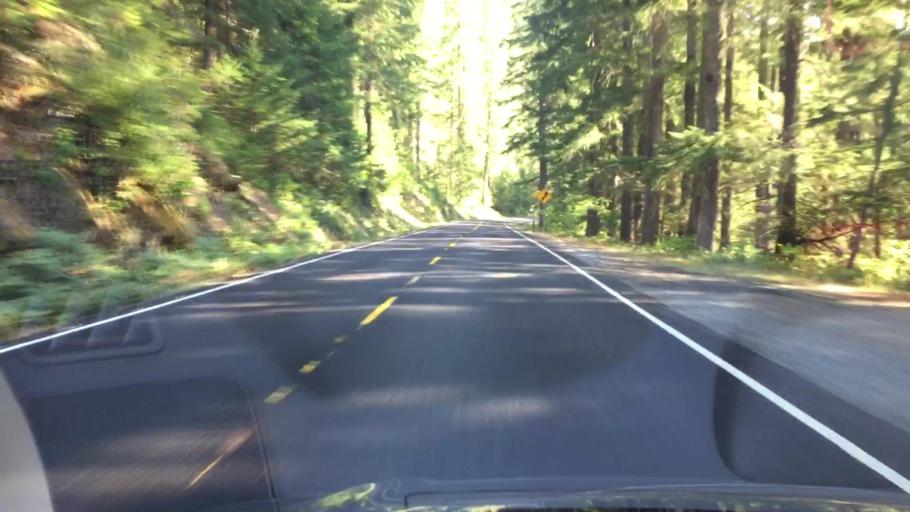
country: US
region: Washington
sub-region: Pierce County
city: Buckley
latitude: 46.7127
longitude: -121.5757
